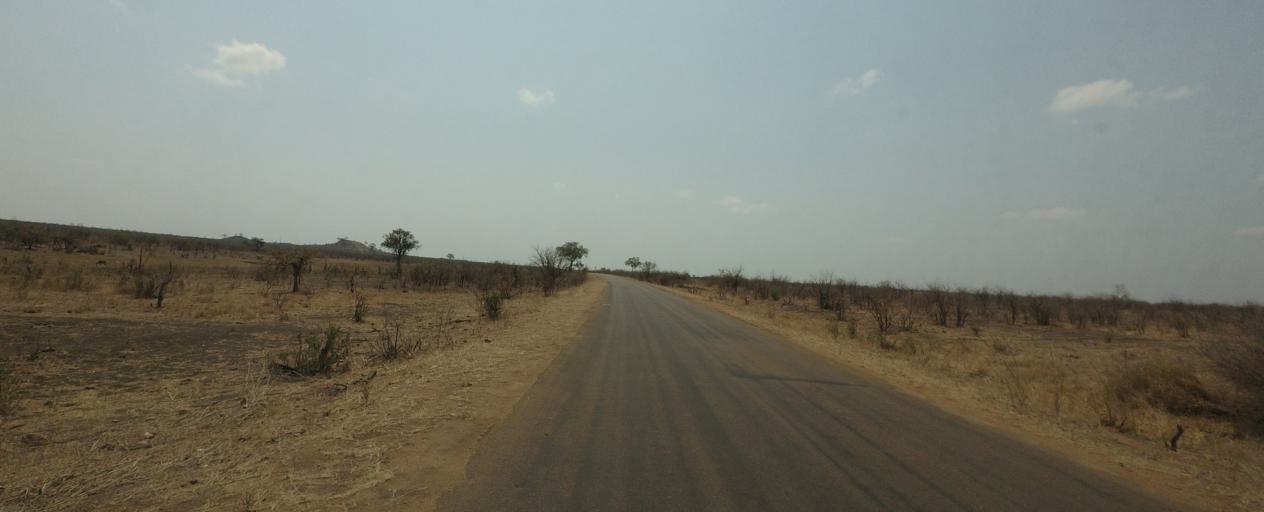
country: ZA
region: Limpopo
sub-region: Mopani District Municipality
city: Phalaborwa
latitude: -23.5045
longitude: 31.4045
